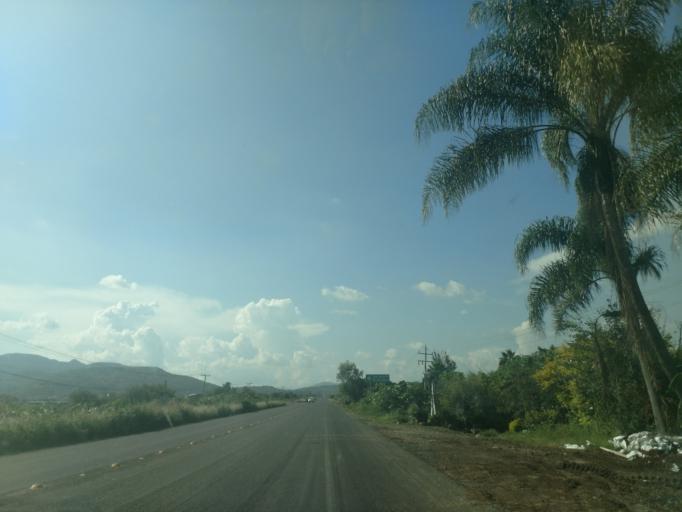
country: MX
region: Jalisco
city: Ahualulco de Mercado
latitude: 20.7148
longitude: -103.9776
